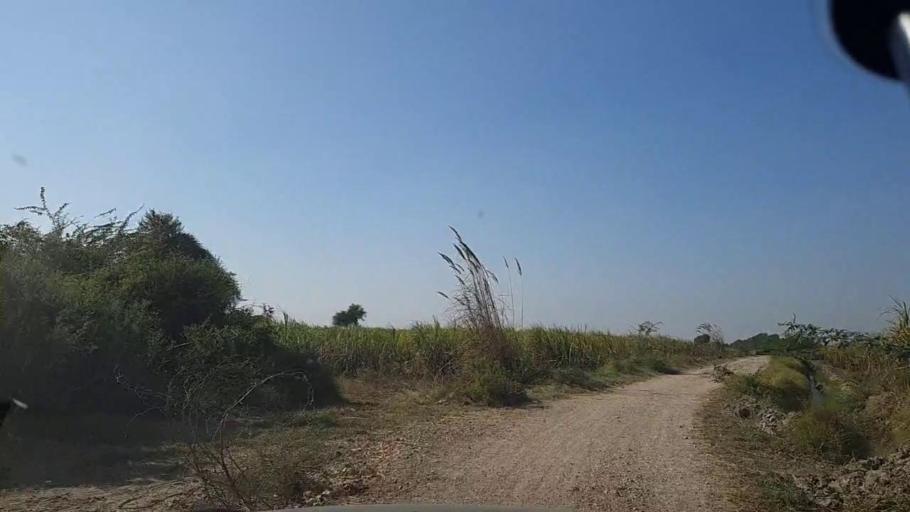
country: PK
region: Sindh
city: Chuhar Jamali
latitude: 24.5745
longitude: 68.0418
